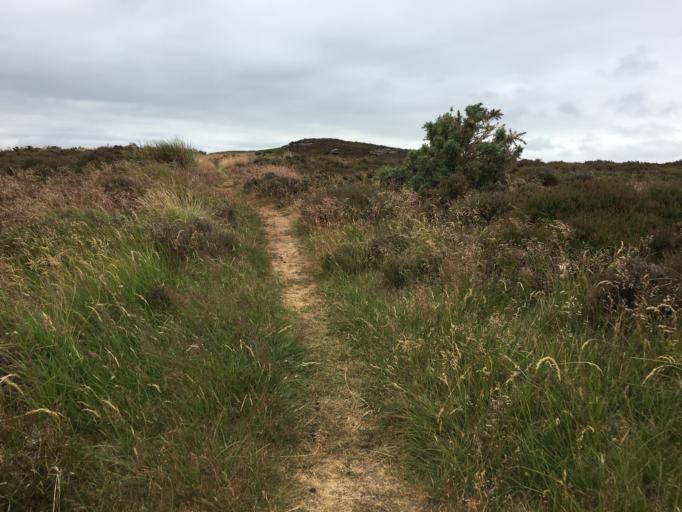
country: GB
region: England
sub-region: Northumberland
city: Lowick
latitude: 55.6138
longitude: -1.9101
